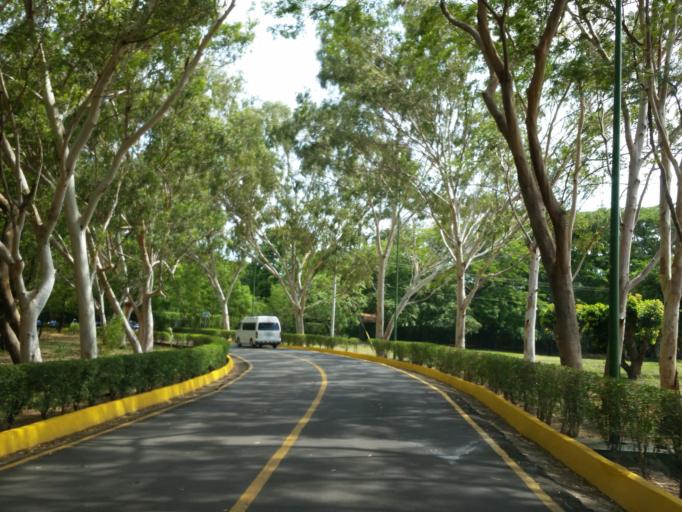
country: NI
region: Managua
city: Masachapa
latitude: 11.8048
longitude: -86.5168
